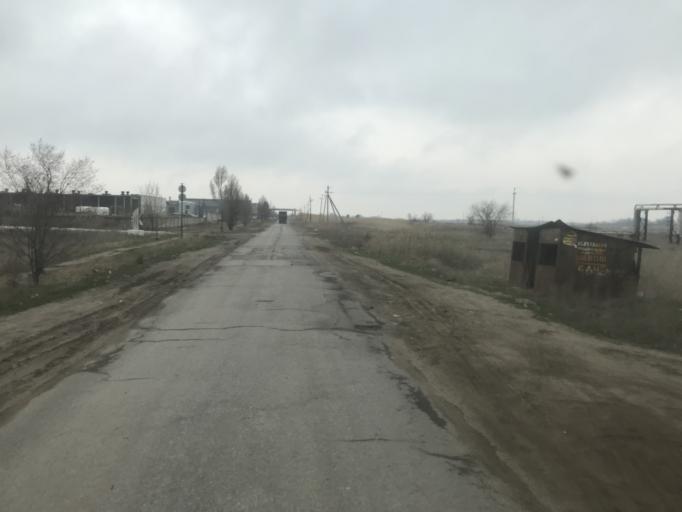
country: RU
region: Volgograd
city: Svetlyy Yar
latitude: 48.5231
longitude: 44.6195
